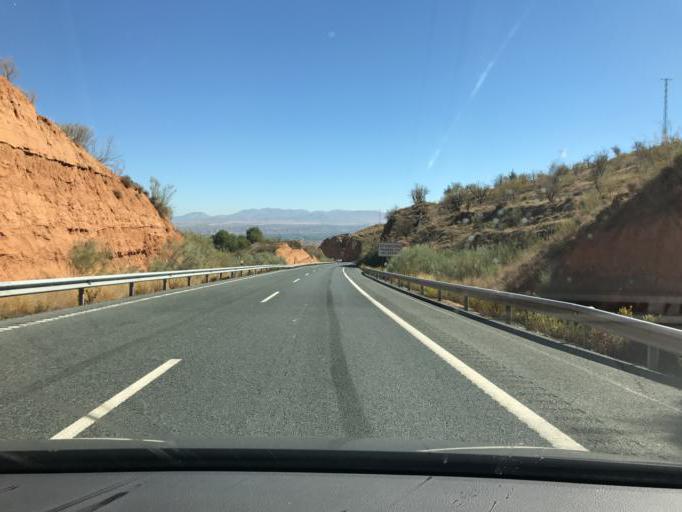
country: ES
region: Andalusia
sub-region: Provincia de Granada
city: Darro
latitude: 37.3238
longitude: -3.2548
